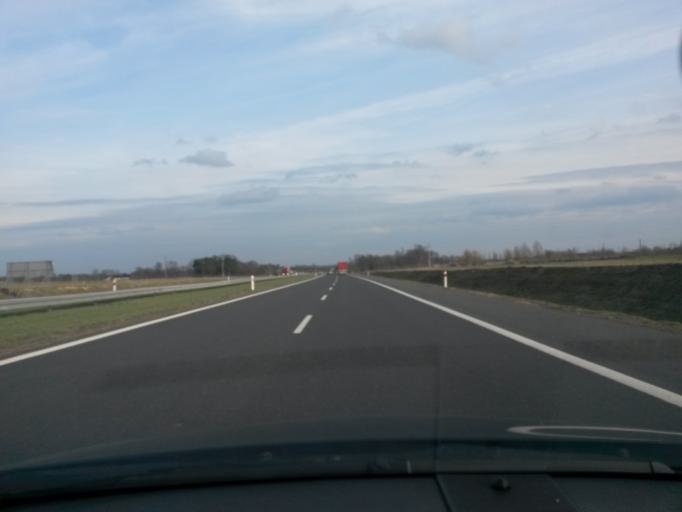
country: PL
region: Lodz Voivodeship
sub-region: Powiat poddebicki
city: Wartkowice
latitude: 51.9771
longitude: 19.0780
